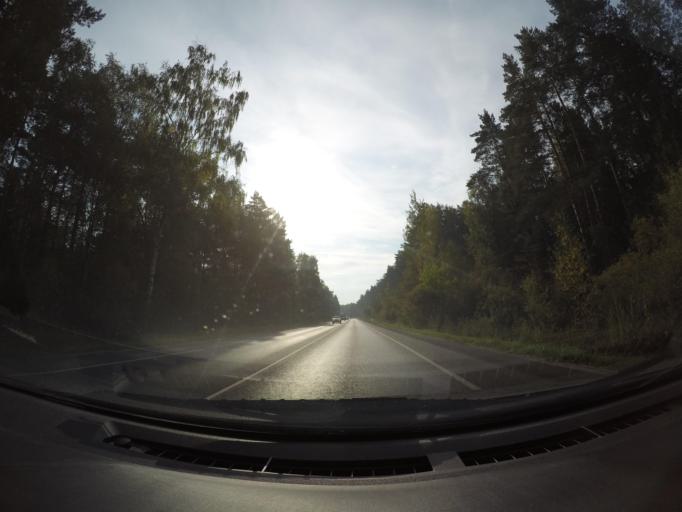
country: RU
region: Moskovskaya
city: Ramenskoye
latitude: 55.6361
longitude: 38.2591
